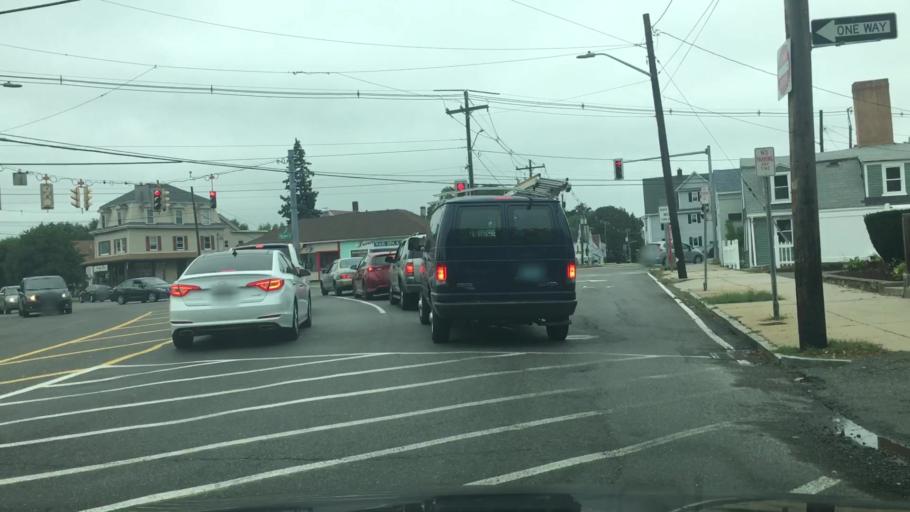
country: US
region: Massachusetts
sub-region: Essex County
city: Peabody
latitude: 42.5336
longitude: -70.9279
